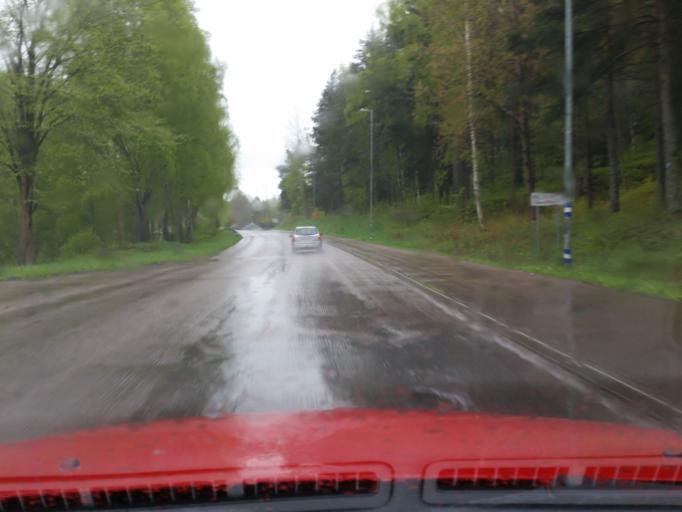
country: SE
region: Dalarna
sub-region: Hedemora Kommun
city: Hedemora
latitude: 60.2894
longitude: 15.9750
